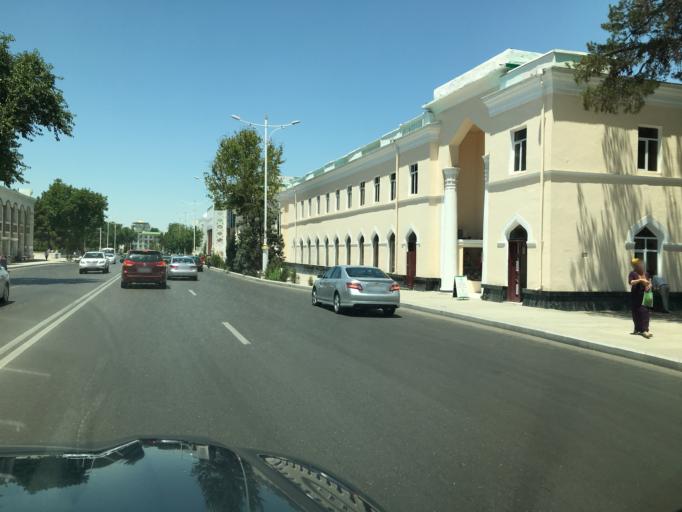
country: TM
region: Ahal
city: Ashgabat
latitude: 37.9399
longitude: 58.3800
